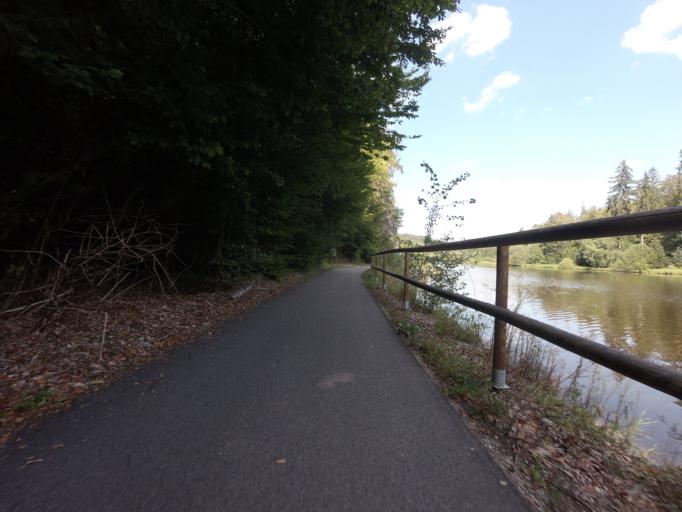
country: CZ
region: Jihocesky
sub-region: Okres Ceske Budejovice
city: Hluboka nad Vltavou
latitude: 49.0768
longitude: 14.4536
